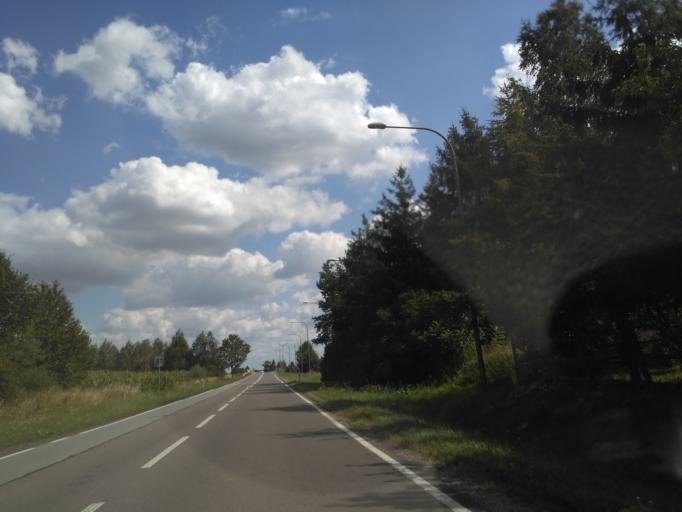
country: PL
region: Lublin Voivodeship
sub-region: Powiat leczynski
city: Puchaczow
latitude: 51.2941
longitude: 23.0057
